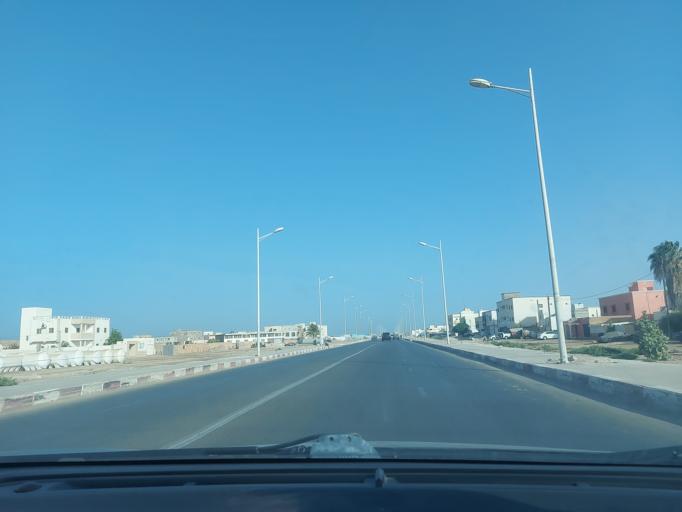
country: MR
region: Nouakchott
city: Nouakchott
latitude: 18.0929
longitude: -16.0124
